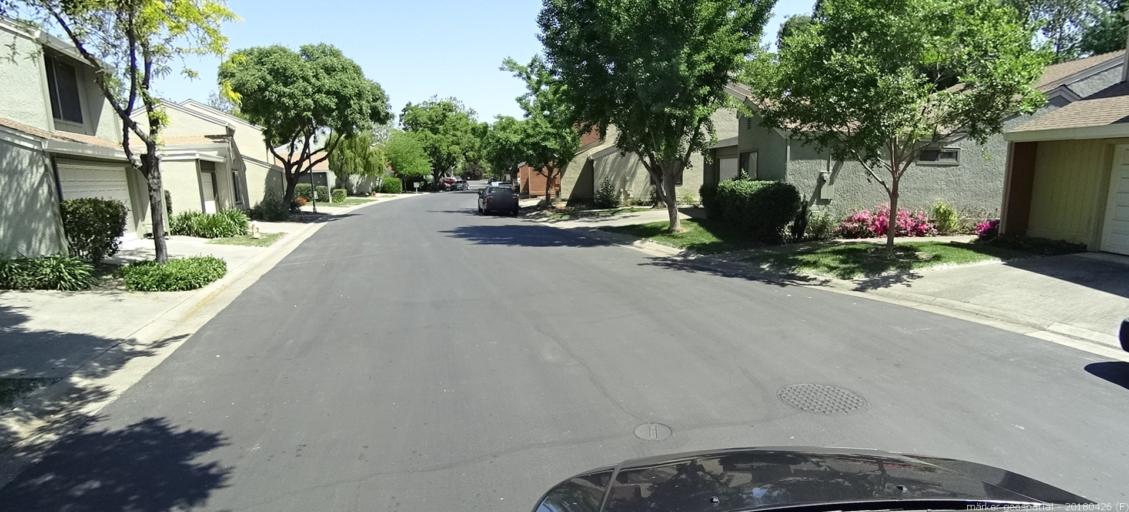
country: US
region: California
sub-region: Yolo County
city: West Sacramento
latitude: 38.5499
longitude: -121.5514
